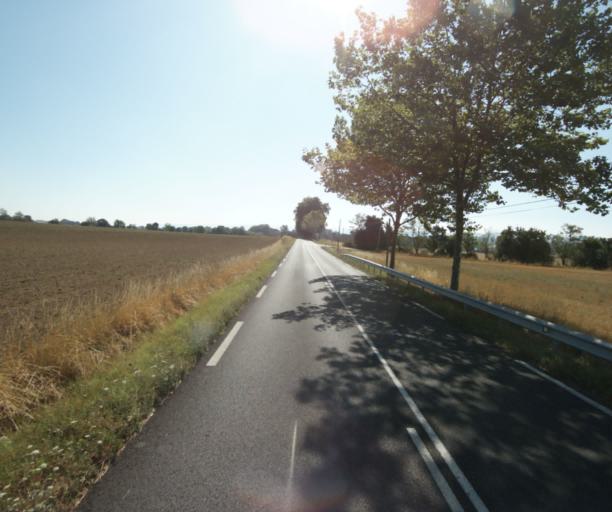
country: FR
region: Midi-Pyrenees
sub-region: Departement de la Haute-Garonne
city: Revel
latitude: 43.4700
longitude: 1.9602
